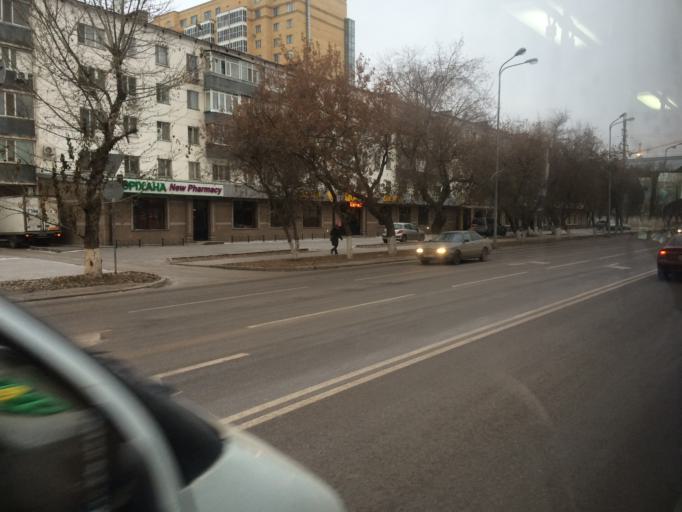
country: KZ
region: Astana Qalasy
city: Astana
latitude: 51.1702
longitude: 71.4391
